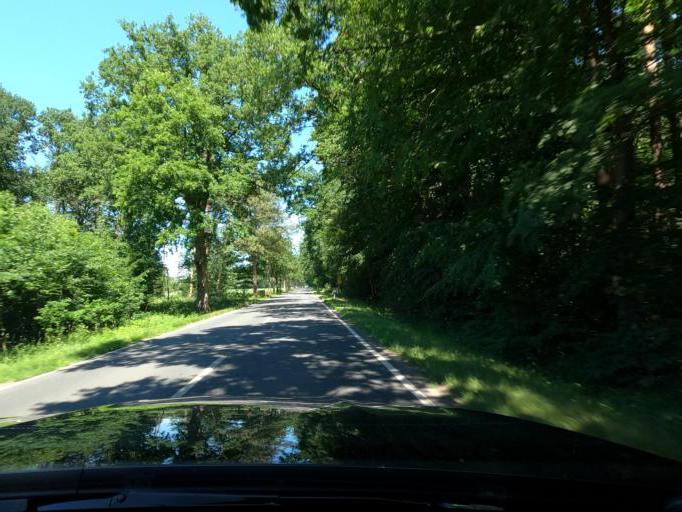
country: DE
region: Lower Saxony
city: Wathlingen
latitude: 52.5165
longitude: 10.1380
